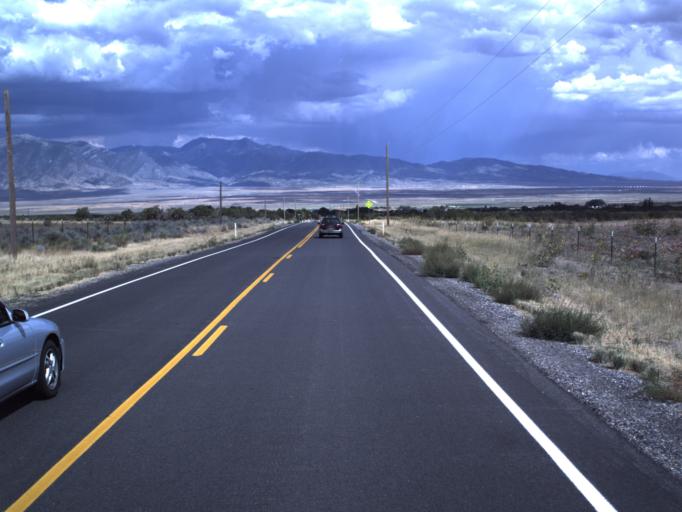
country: US
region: Utah
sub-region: Tooele County
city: Grantsville
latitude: 40.3361
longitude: -112.5021
